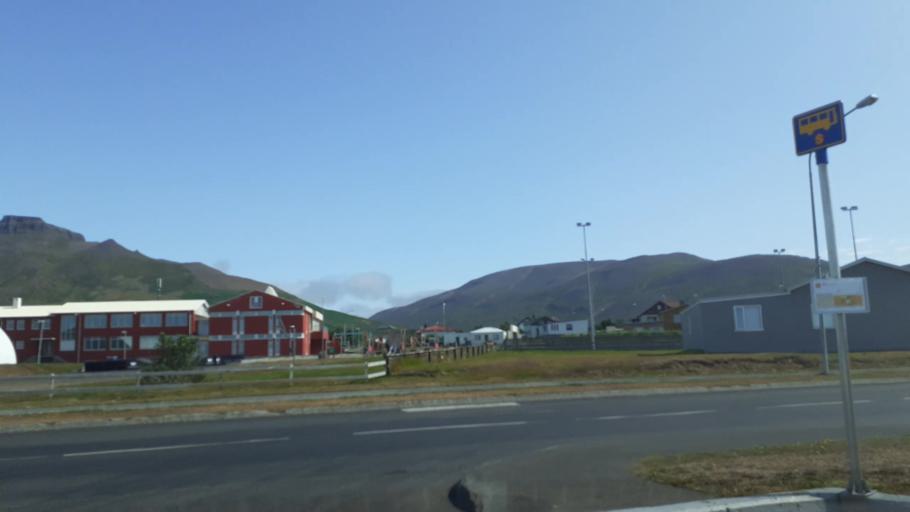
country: IS
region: Northwest
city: Saudarkrokur
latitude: 65.8235
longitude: -20.3057
